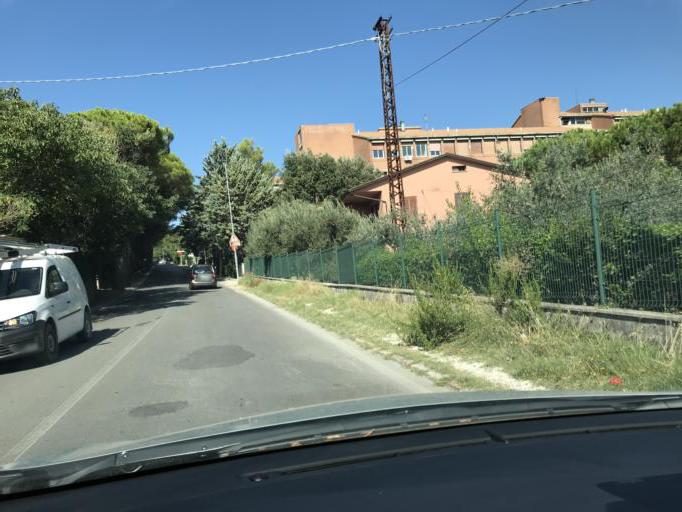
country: IT
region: Umbria
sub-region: Provincia di Perugia
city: Perugia
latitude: 43.1115
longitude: 12.4059
